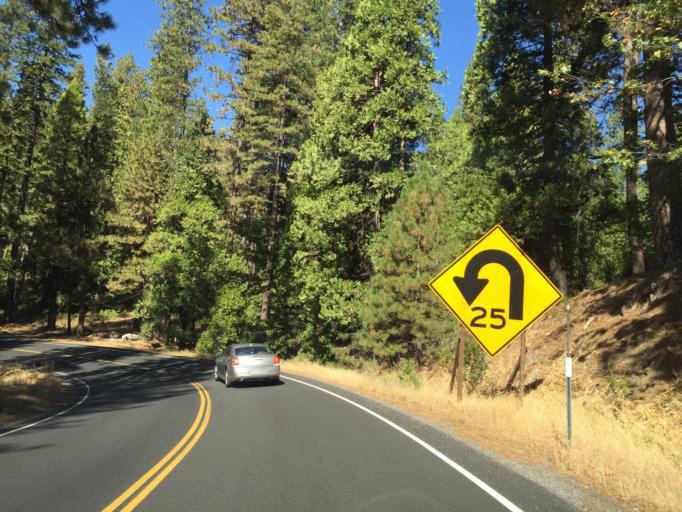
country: US
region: California
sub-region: Tuolumne County
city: Twain Harte
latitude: 38.0465
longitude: -120.2088
